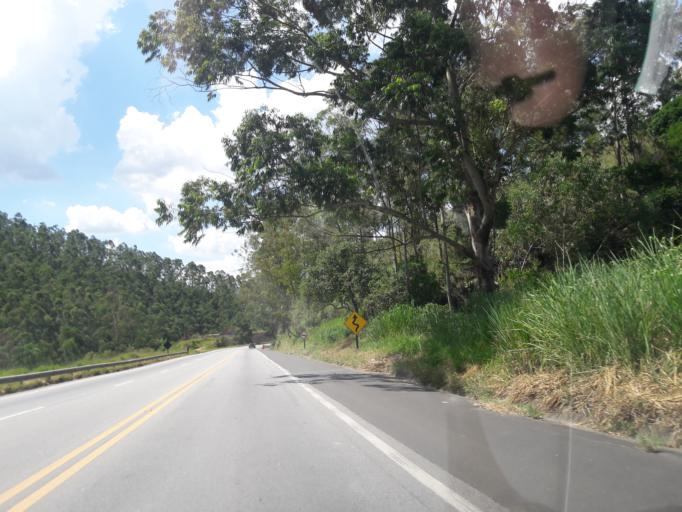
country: BR
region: Sao Paulo
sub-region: Campo Limpo Paulista
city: Campo Limpo Paulista
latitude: -23.2544
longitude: -46.7916
